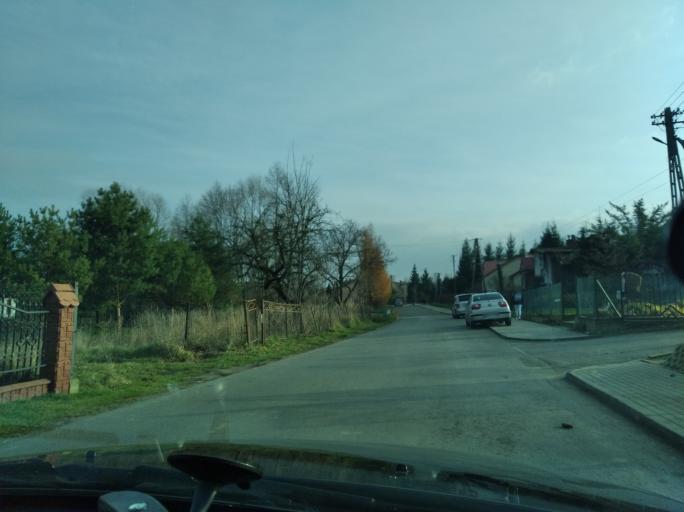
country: PL
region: Subcarpathian Voivodeship
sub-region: Powiat przeworski
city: Siedleczka
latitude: 49.9609
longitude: 22.3791
